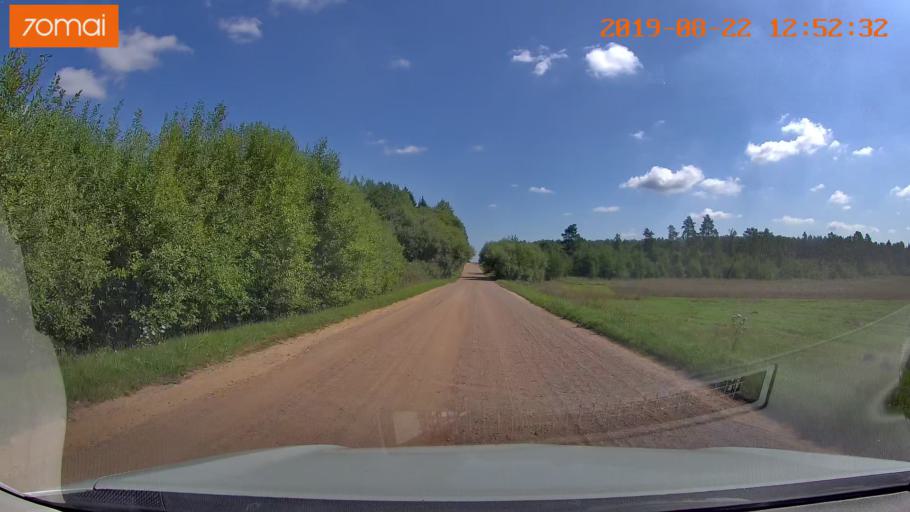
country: BY
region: Minsk
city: Prawdzinski
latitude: 53.4516
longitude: 27.6738
